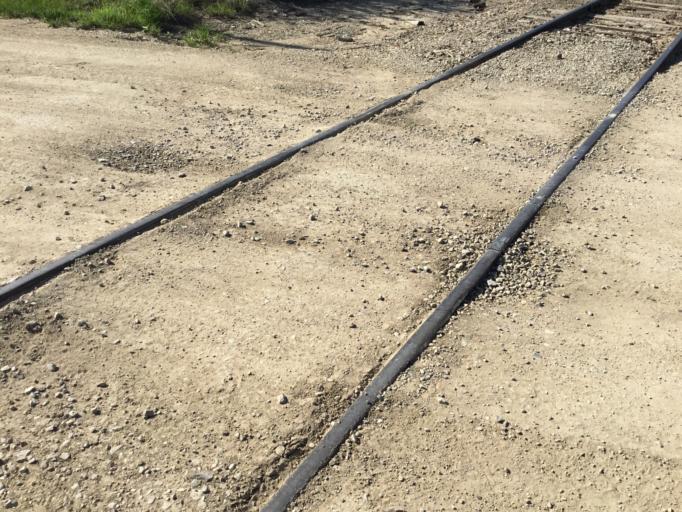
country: US
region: Kansas
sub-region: Mitchell County
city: Beloit
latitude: 39.4663
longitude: -98.0478
